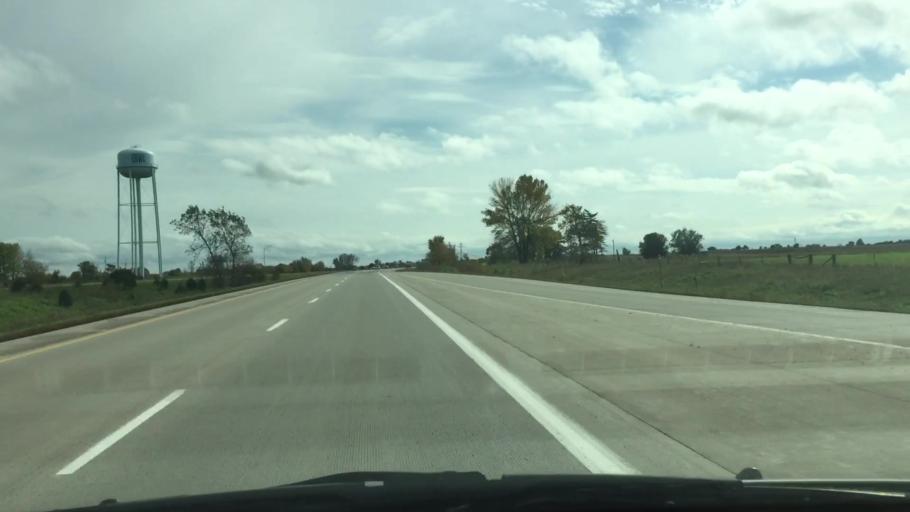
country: US
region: Iowa
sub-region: Clarke County
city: Osceola
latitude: 40.9898
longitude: -93.7985
